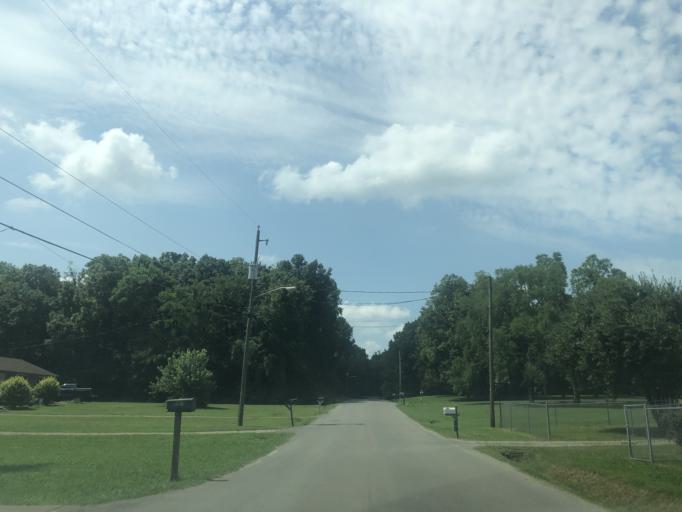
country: US
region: Tennessee
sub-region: Rutherford County
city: La Vergne
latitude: 36.0111
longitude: -86.5870
